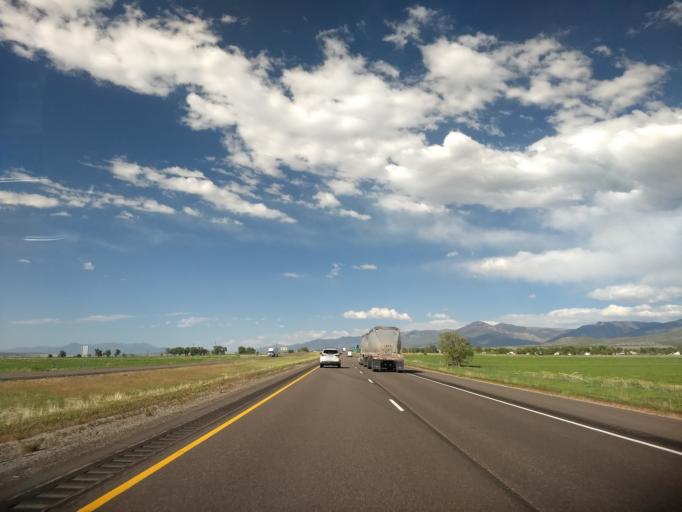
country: US
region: Utah
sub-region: Millard County
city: Fillmore
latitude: 38.8817
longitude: -112.4259
